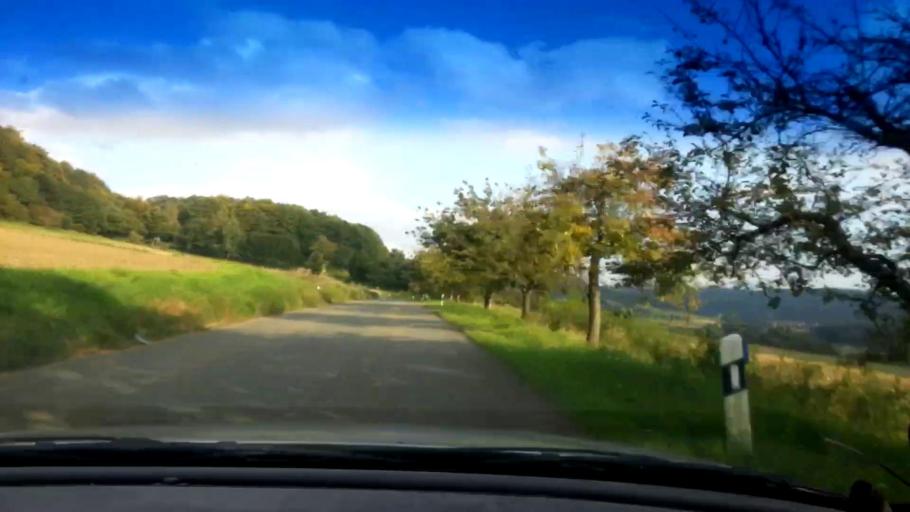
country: DE
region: Bavaria
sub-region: Upper Franconia
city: Schesslitz
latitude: 50.0095
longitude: 11.0521
